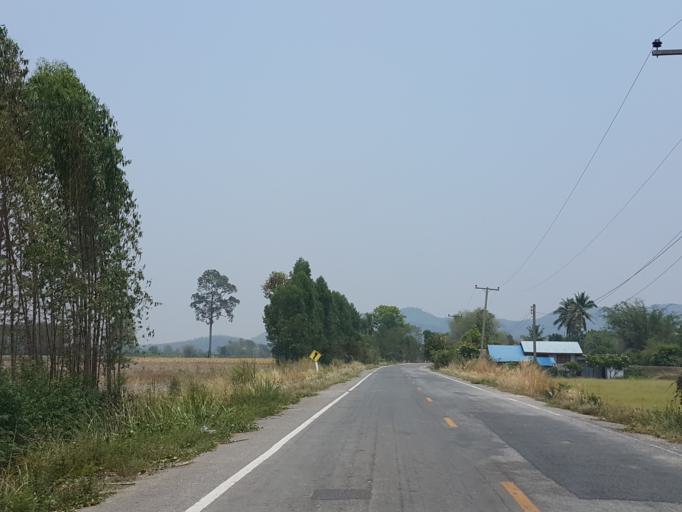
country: TH
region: Kamphaeng Phet
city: Pang Sila Thong
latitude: 16.0554
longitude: 99.3622
